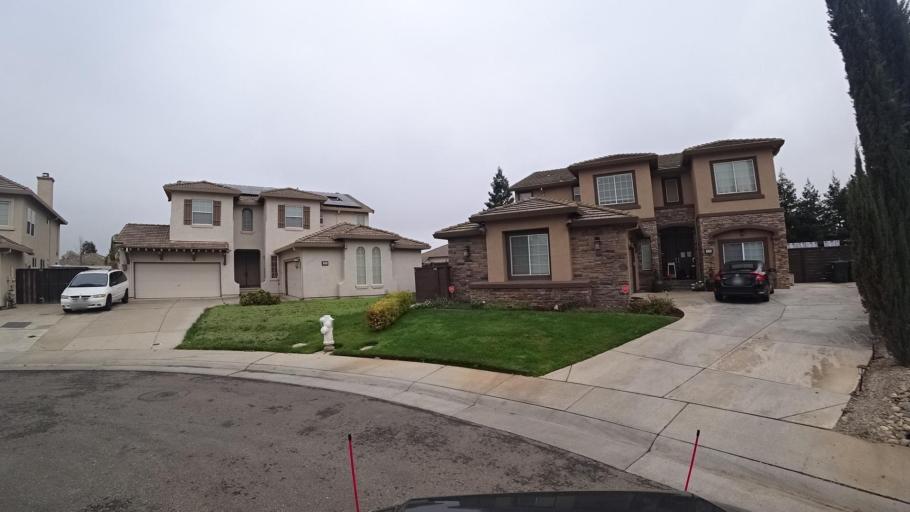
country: US
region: California
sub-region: Sacramento County
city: Elk Grove
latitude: 38.4041
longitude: -121.3401
